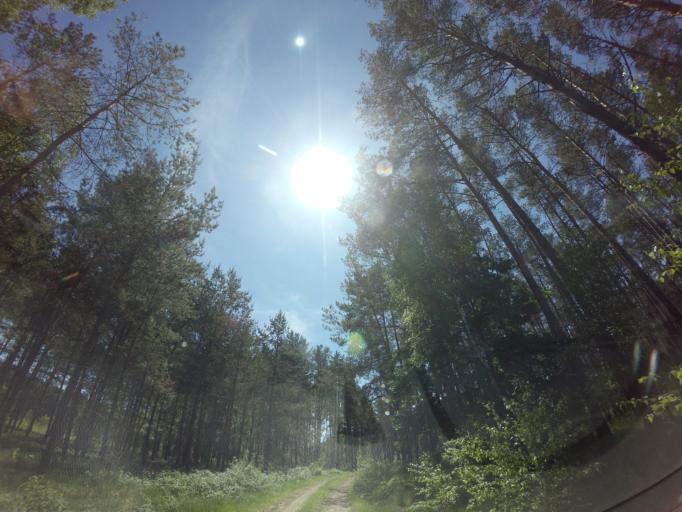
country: PL
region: West Pomeranian Voivodeship
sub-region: Powiat choszczenski
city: Drawno
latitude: 53.2738
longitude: 15.7367
